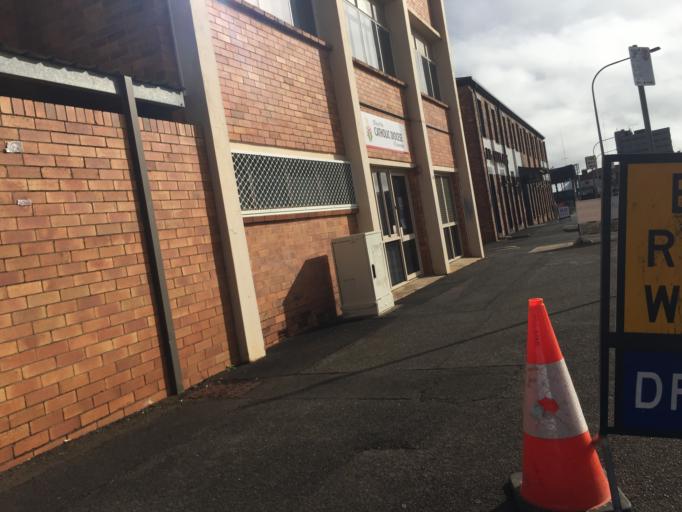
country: AU
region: Queensland
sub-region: Toowoomba
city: Toowoomba
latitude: -27.5629
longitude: 151.9541
